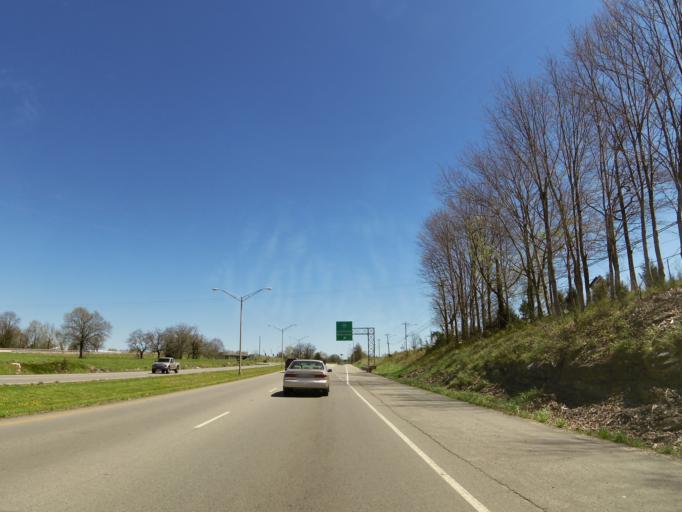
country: US
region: Kentucky
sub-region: Warren County
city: Bowling Green
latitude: 37.0103
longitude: -86.3870
